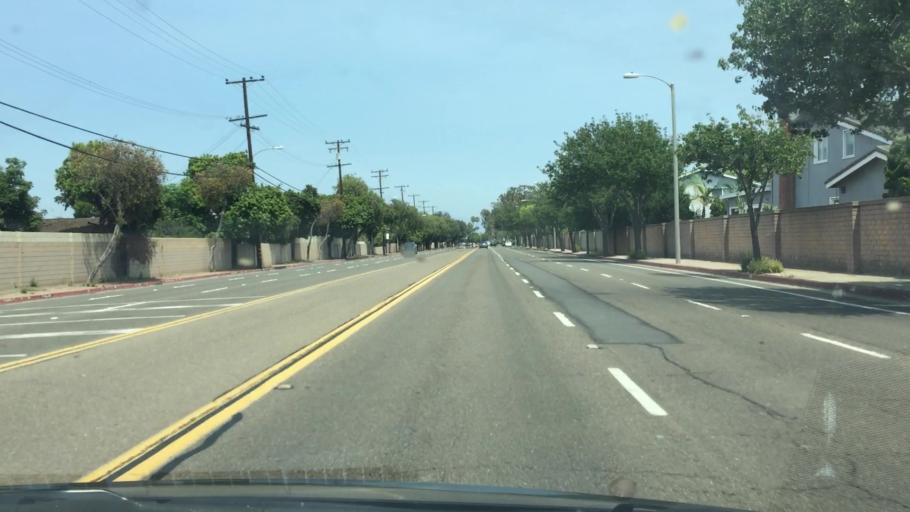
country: US
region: California
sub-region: Orange County
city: Costa Mesa
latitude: 33.6725
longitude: -117.9327
